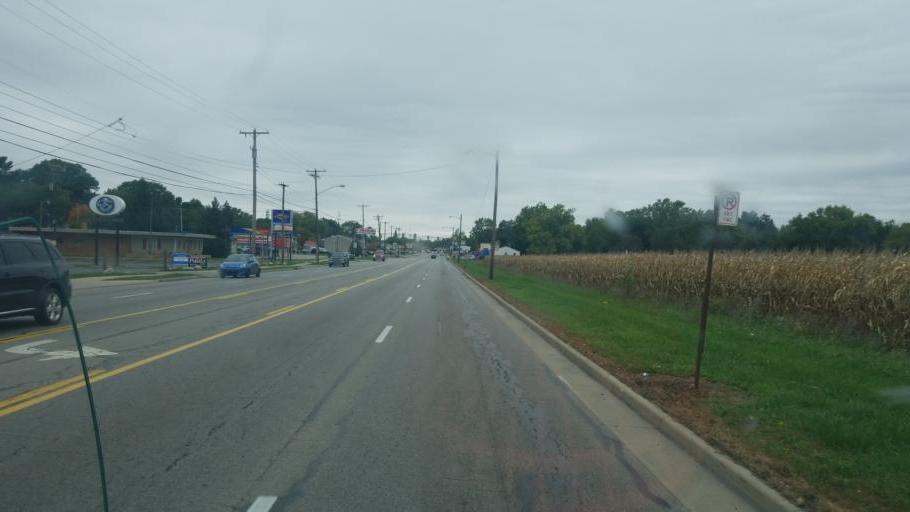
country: US
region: Ohio
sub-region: Lucas County
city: Ottawa Hills
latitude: 41.6441
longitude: -83.6645
